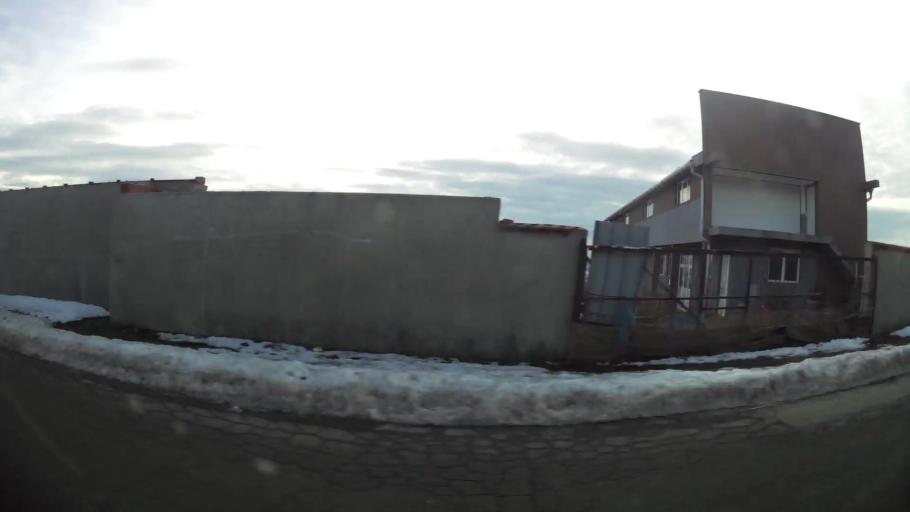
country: RS
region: Central Serbia
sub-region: Belgrade
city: Zvezdara
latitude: 44.7265
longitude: 20.5064
